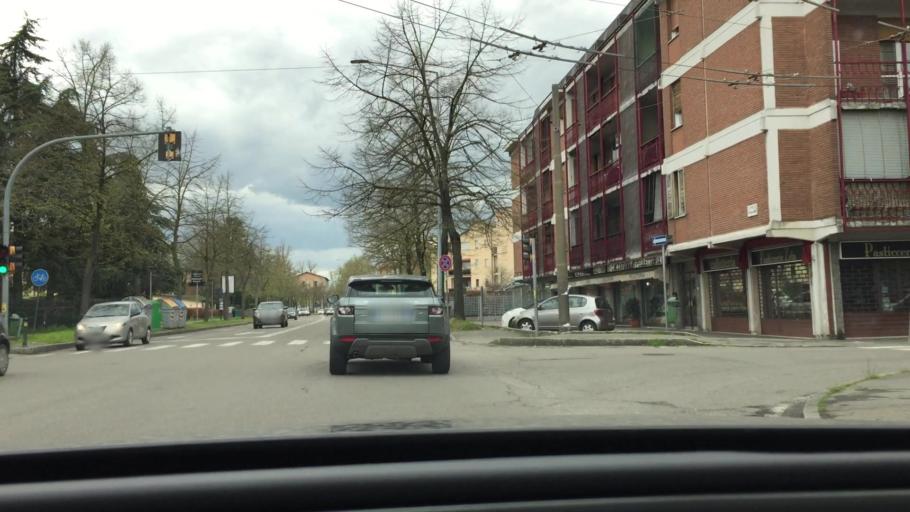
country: IT
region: Emilia-Romagna
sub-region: Provincia di Modena
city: Modena
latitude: 44.6317
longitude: 10.9003
